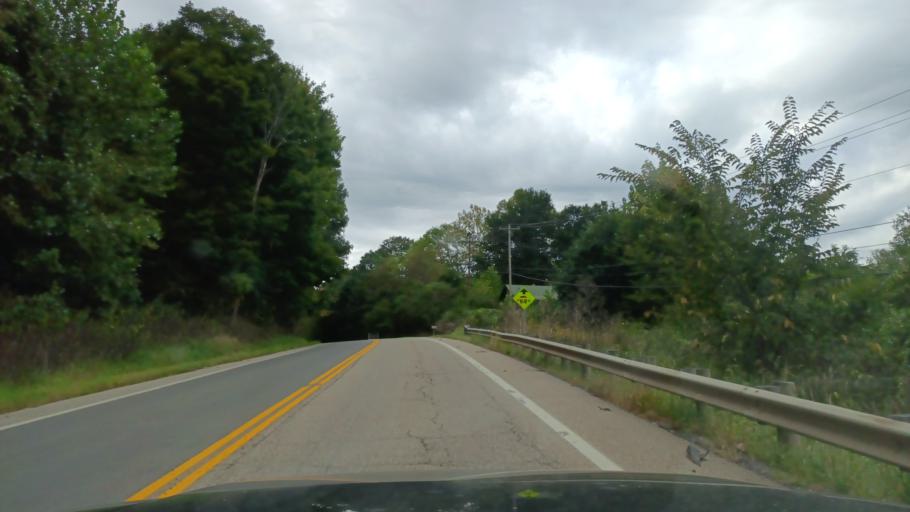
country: US
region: Ohio
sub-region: Vinton County
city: McArthur
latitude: 39.2452
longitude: -82.4605
